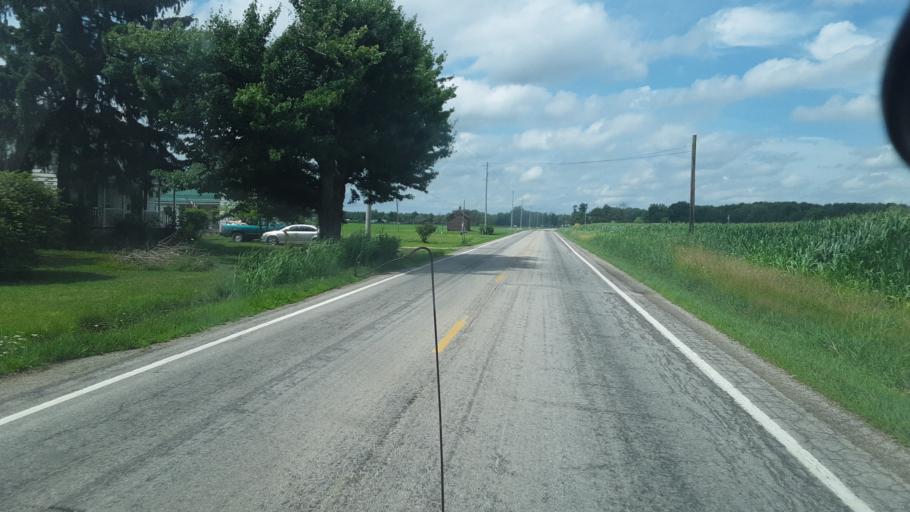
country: US
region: Ohio
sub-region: Ashtabula County
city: Andover
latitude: 41.6665
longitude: -80.6674
